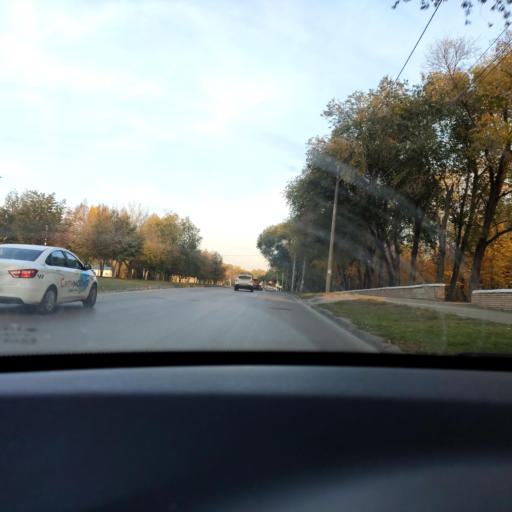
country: RU
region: Samara
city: Samara
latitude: 53.2215
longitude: 50.2377
